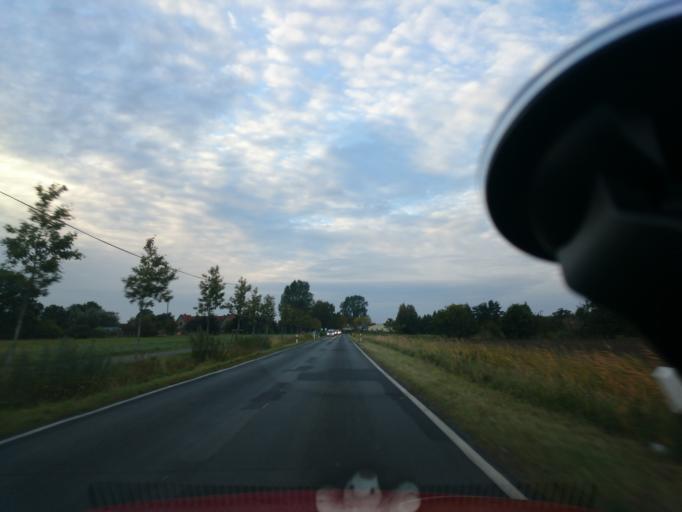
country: DE
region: Mecklenburg-Vorpommern
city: Zingst
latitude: 54.3706
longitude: 12.6291
